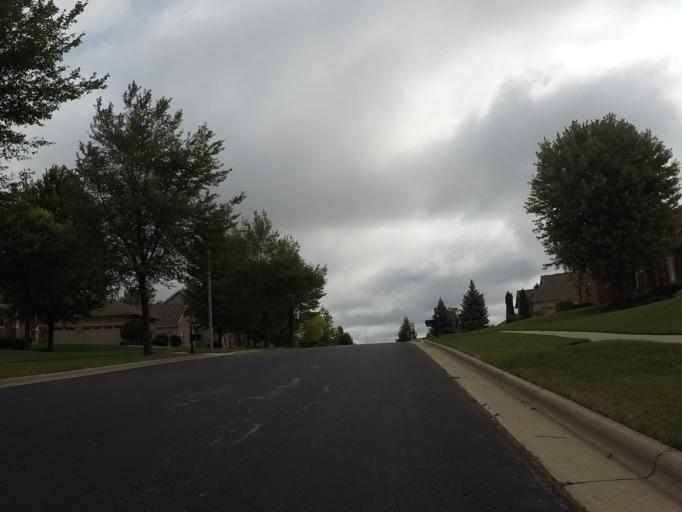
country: US
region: Wisconsin
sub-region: Dane County
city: Verona
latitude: 43.0400
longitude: -89.5466
